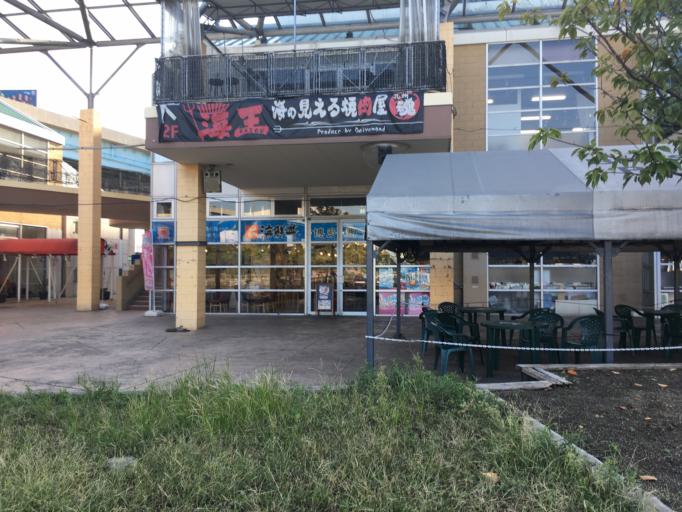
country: JP
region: Fukuoka
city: Fukuoka-shi
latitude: 33.6036
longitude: 130.3992
